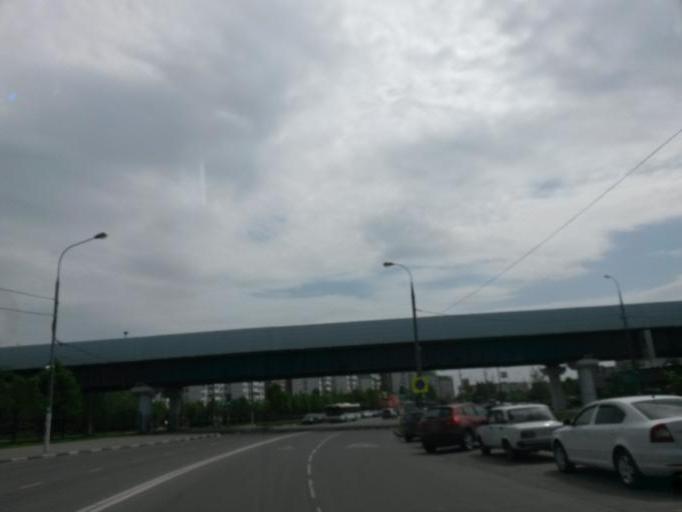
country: RU
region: Moskovskaya
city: Kommunarka
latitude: 55.5429
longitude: 37.5321
